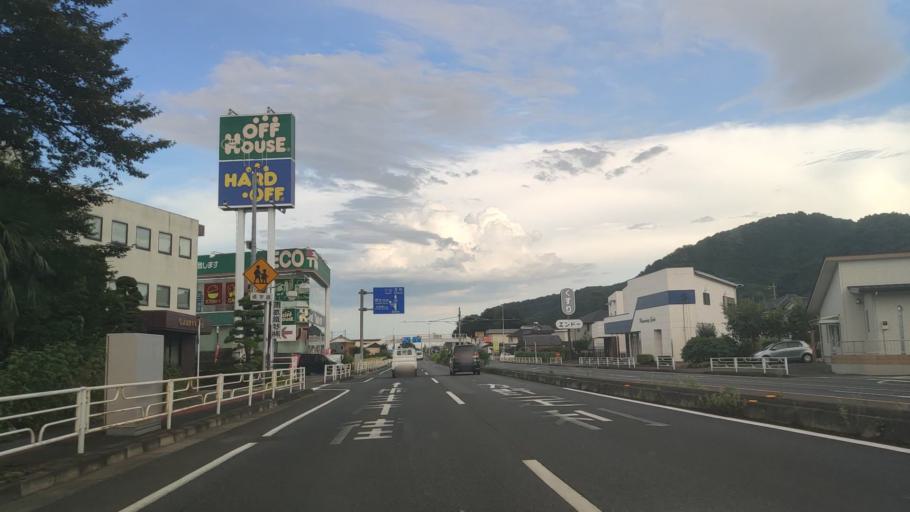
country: JP
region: Gunma
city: Kiryu
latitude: 36.3742
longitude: 139.3503
